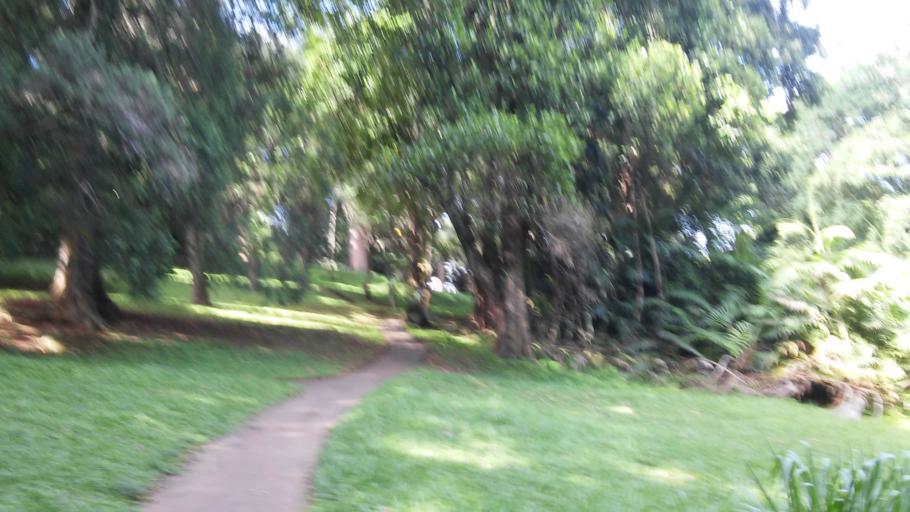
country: LK
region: Central
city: Kandy
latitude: 7.2680
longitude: 80.5954
